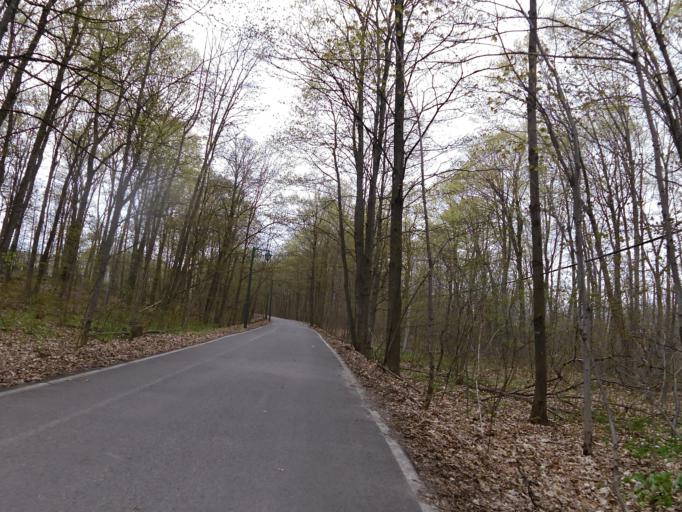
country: CA
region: Quebec
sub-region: Laurentides
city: Deux-Montagnes
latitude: 45.5442
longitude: -73.9127
